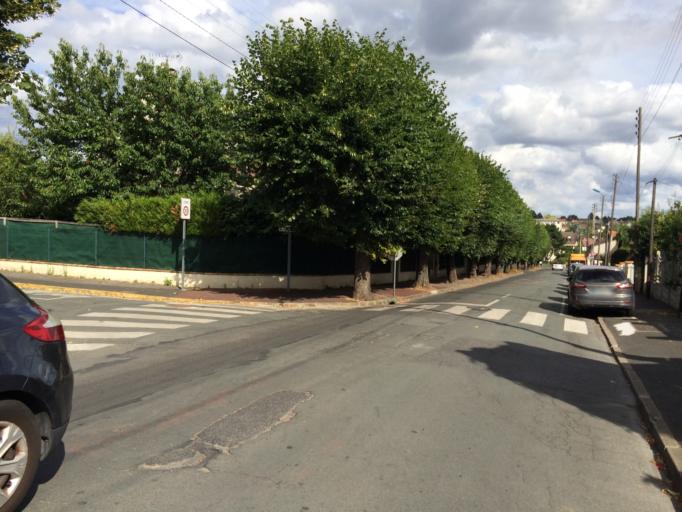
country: FR
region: Ile-de-France
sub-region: Departement de l'Essonne
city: Longjumeau
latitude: 48.6992
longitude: 2.3209
